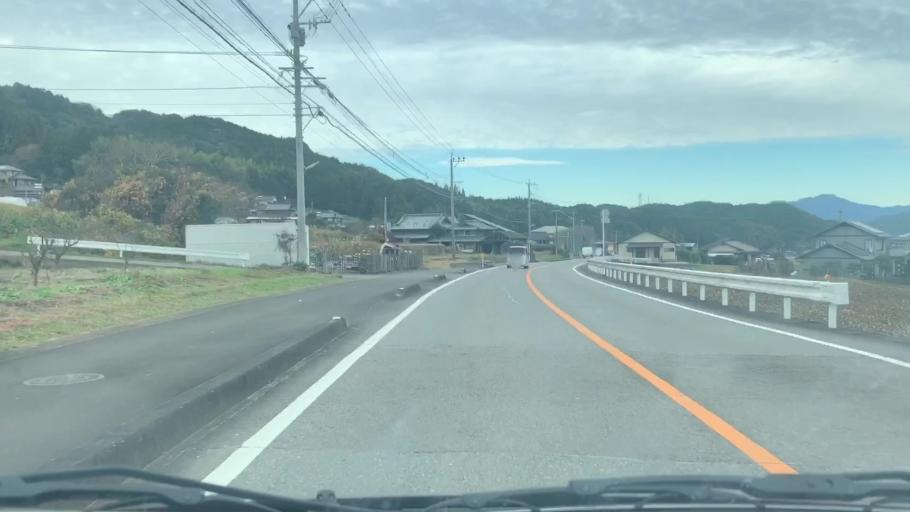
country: JP
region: Saga Prefecture
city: Takeocho-takeo
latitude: 33.1711
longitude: 129.9693
